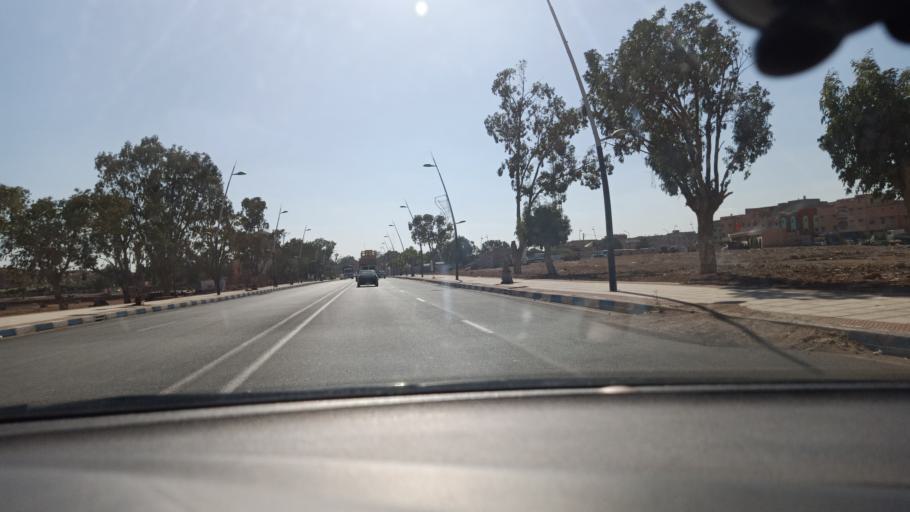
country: MA
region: Doukkala-Abda
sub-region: Safi
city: Youssoufia
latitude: 32.0831
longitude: -8.6207
